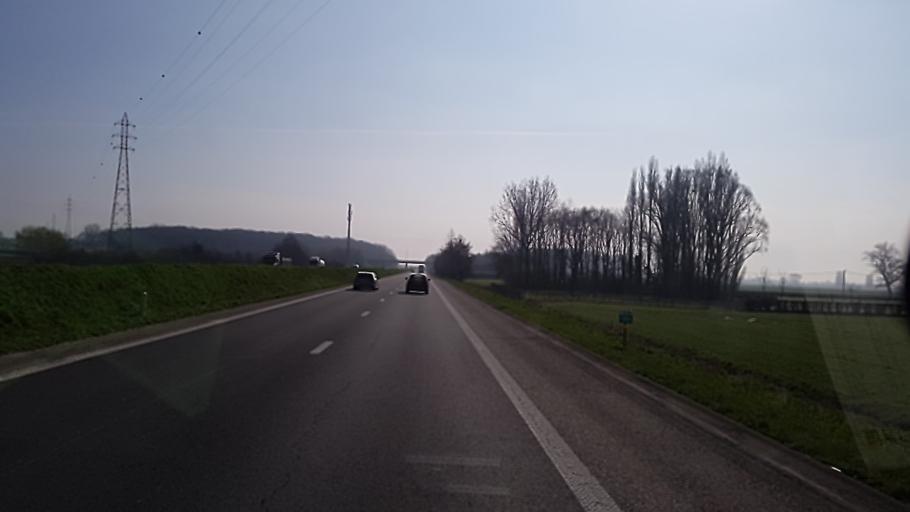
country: BE
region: Flanders
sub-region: Provincie West-Vlaanderen
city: Wervik
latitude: 50.8291
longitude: 3.0406
